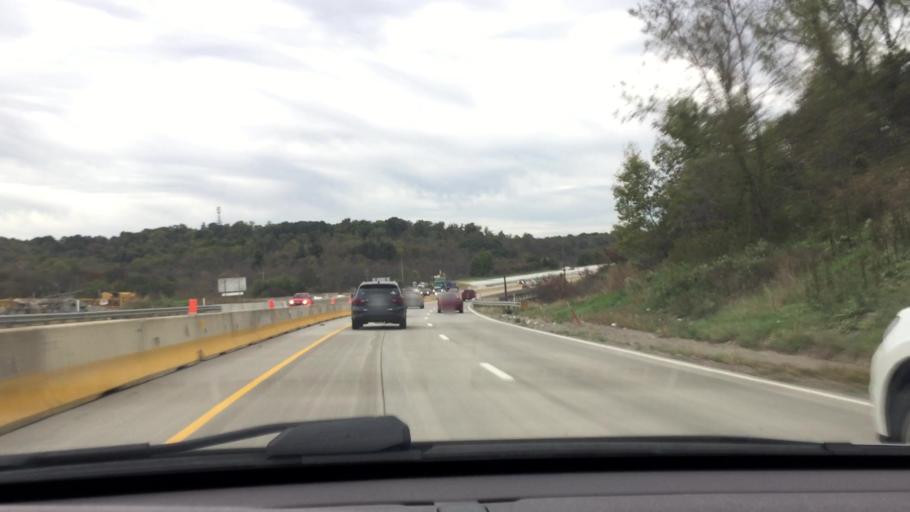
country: US
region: Pennsylvania
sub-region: Allegheny County
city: Enlow
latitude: 40.4678
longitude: -80.2391
